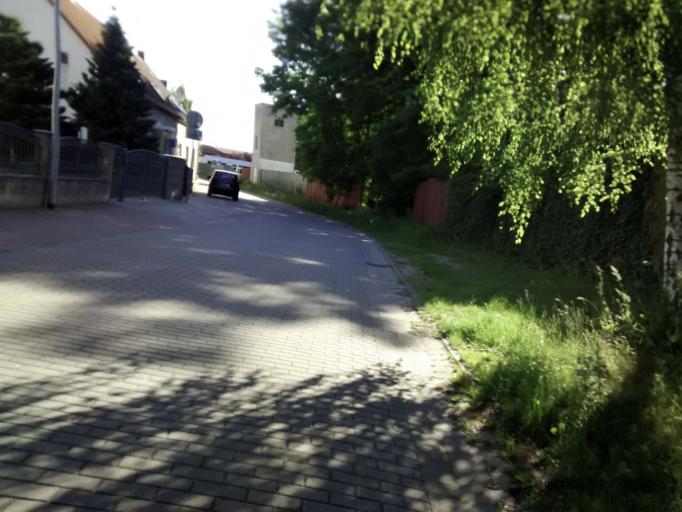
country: DE
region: Saxony-Anhalt
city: Rogatz
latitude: 52.3168
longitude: 11.7717
